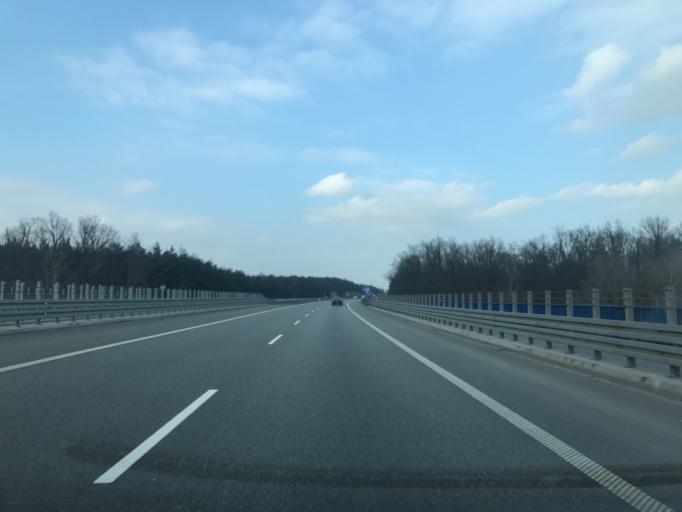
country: PL
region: Kujawsko-Pomorskie
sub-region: Powiat torunski
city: Lubicz Dolny
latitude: 53.0007
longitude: 18.7325
